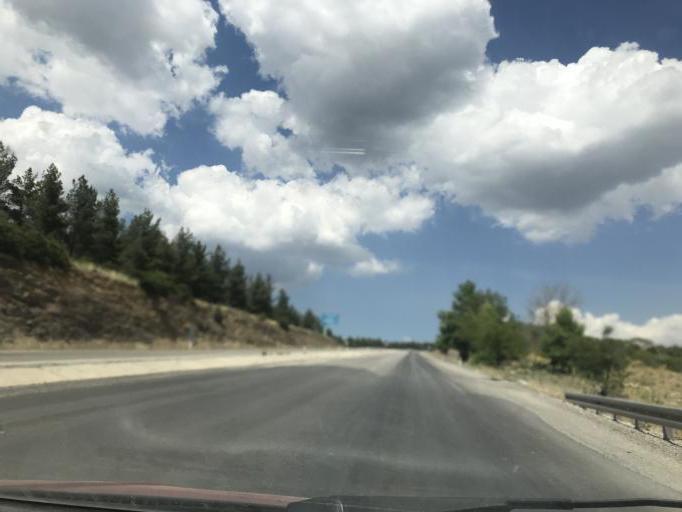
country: TR
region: Denizli
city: Tavas
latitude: 37.5768
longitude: 29.0874
